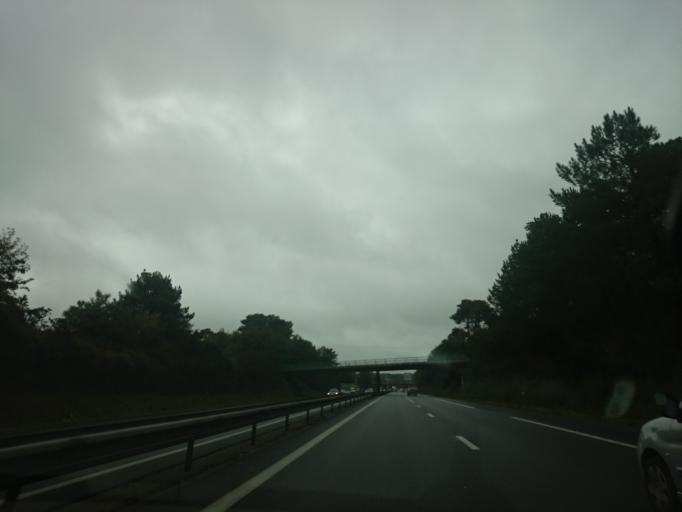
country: FR
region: Brittany
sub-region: Departement du Morbihan
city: Pluneret
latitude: 47.6650
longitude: -2.9584
